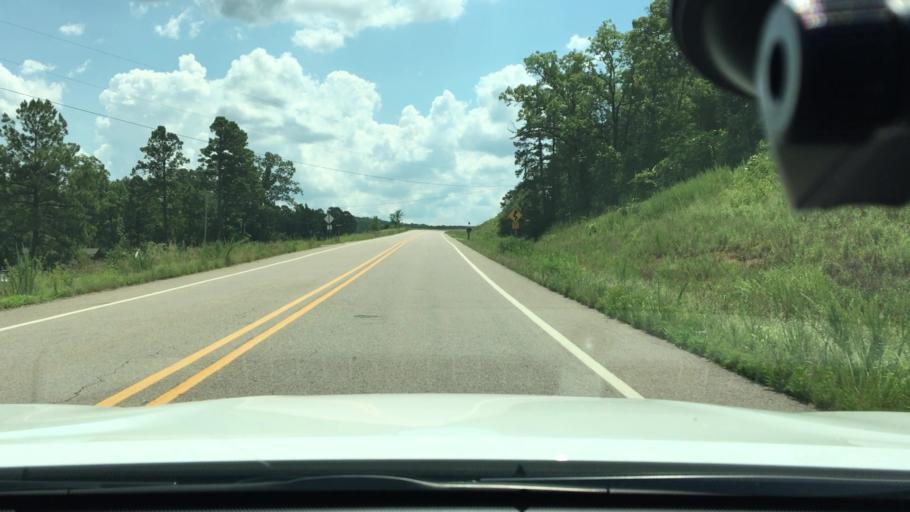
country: US
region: Arkansas
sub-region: Logan County
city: Paris
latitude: 35.2563
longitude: -93.6804
